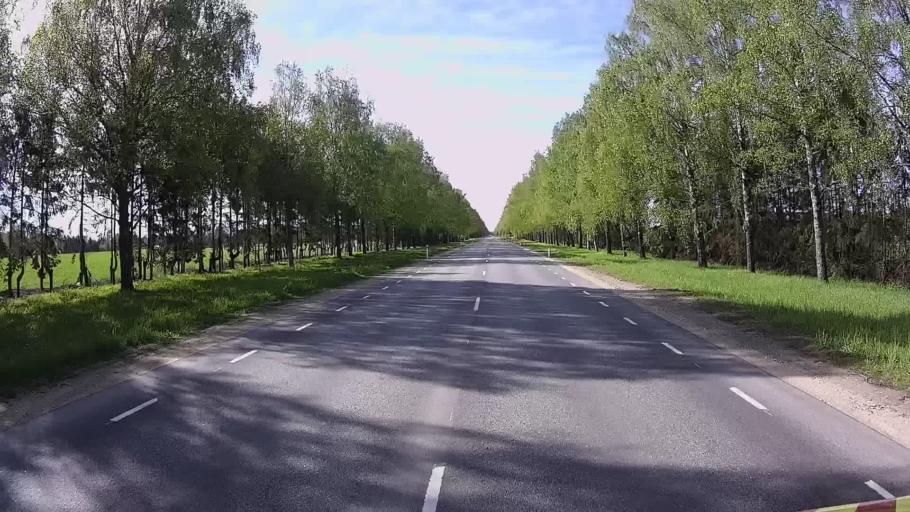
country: EE
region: Polvamaa
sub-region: Polva linn
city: Polva
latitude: 58.3028
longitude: 27.0011
